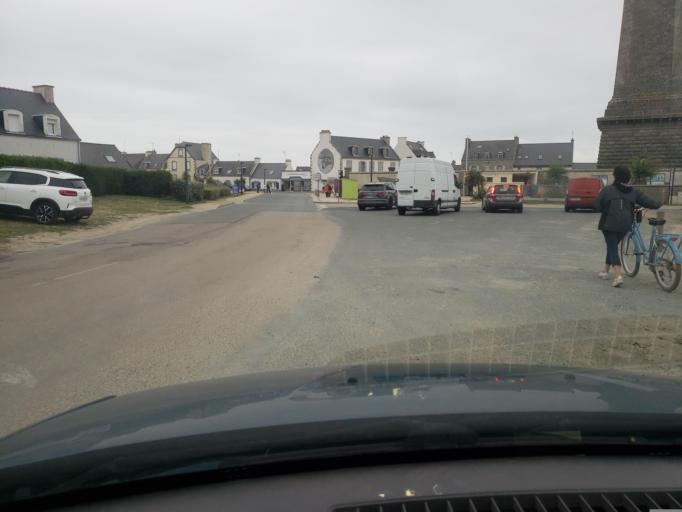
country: FR
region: Brittany
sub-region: Departement du Finistere
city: Guilvinec
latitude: 47.7990
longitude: -4.3731
